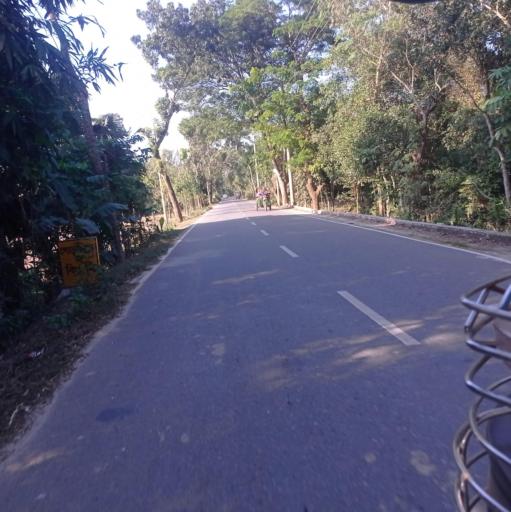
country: BD
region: Dhaka
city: Bajitpur
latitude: 24.1456
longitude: 90.8150
